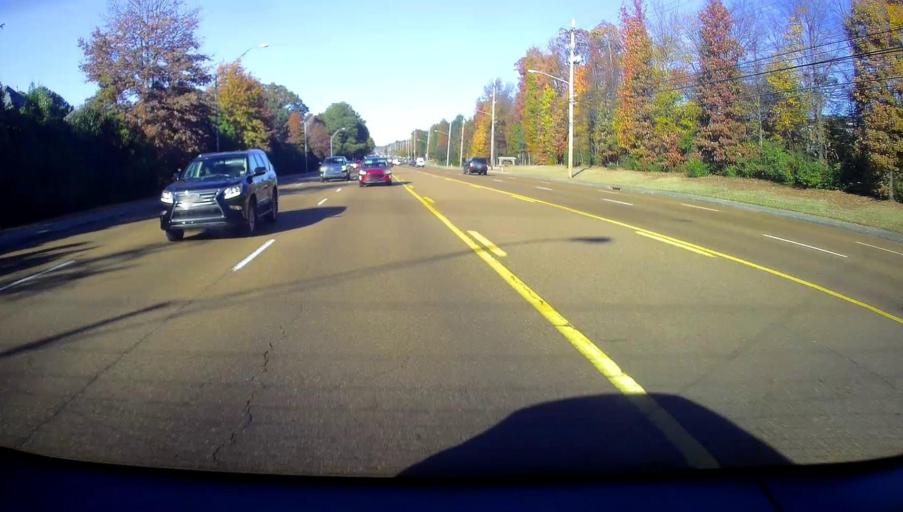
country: US
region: Tennessee
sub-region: Shelby County
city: Germantown
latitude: 35.1052
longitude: -89.8041
